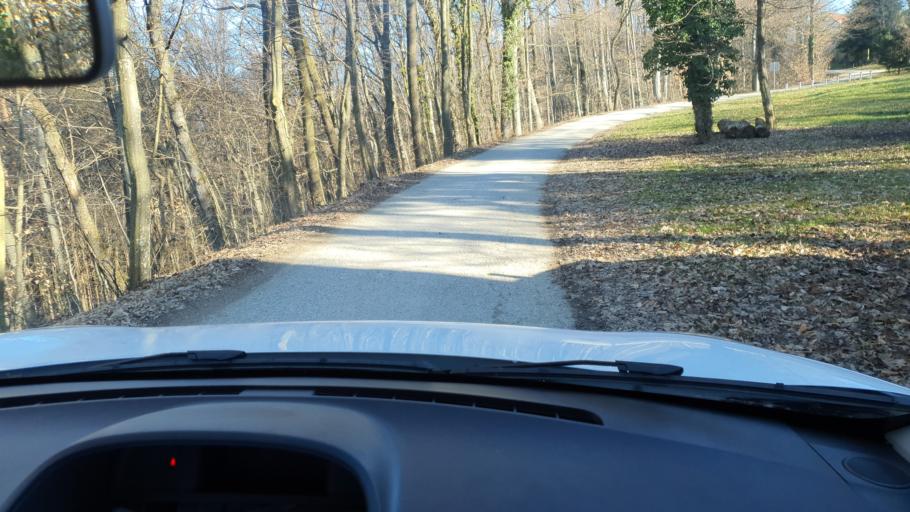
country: SI
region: Sveti Andraz v Slovenskih Goricah
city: Vitomarci
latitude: 46.5255
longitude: 15.9304
